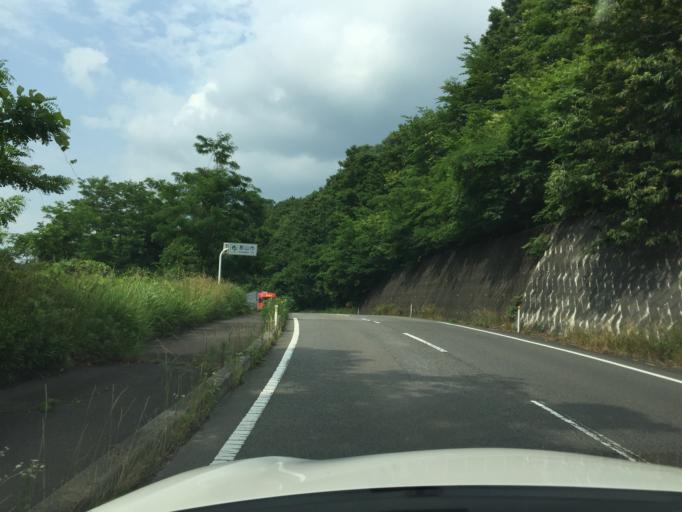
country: JP
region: Fukushima
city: Sukagawa
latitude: 37.3053
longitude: 140.4407
